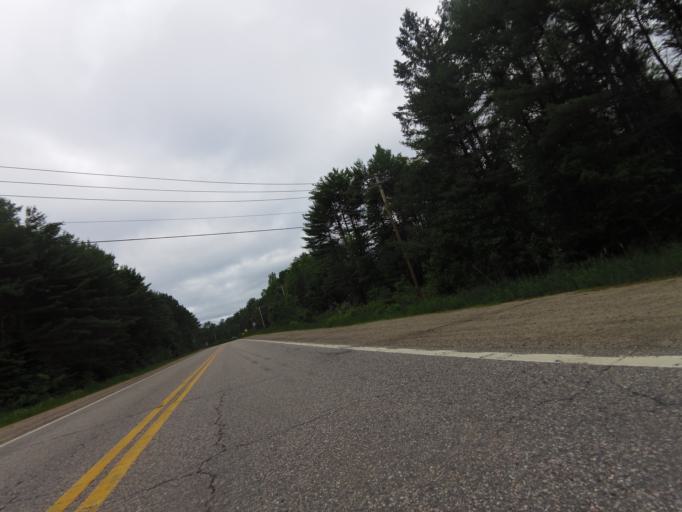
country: CA
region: Quebec
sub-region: Outaouais
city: Shawville
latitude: 45.8585
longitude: -76.4187
